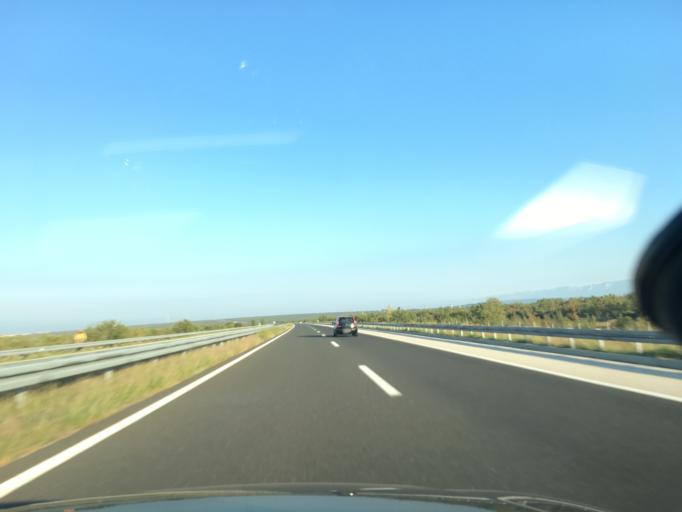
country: HR
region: Zadarska
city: Benkovac
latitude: 43.9846
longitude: 15.6320
